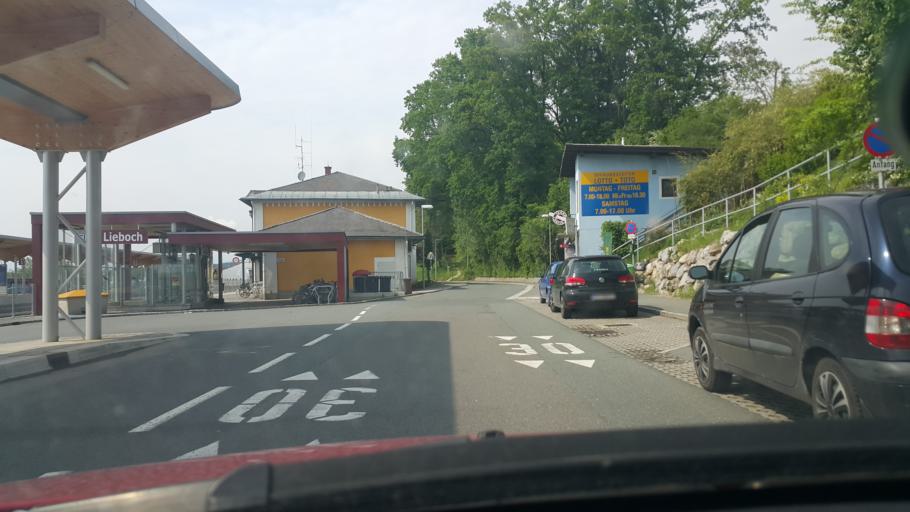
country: AT
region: Styria
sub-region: Politischer Bezirk Graz-Umgebung
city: Lieboch
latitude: 46.9682
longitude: 15.3462
